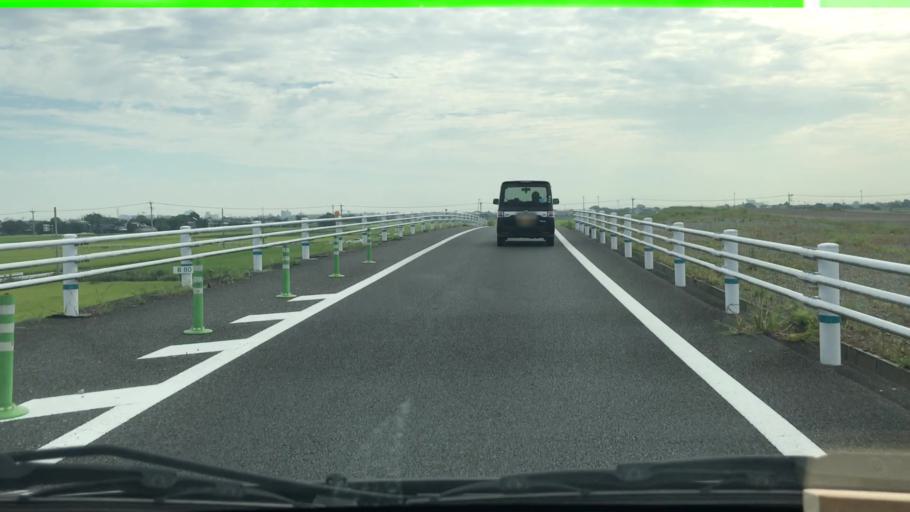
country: JP
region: Saga Prefecture
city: Saga-shi
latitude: 33.2317
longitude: 130.2553
